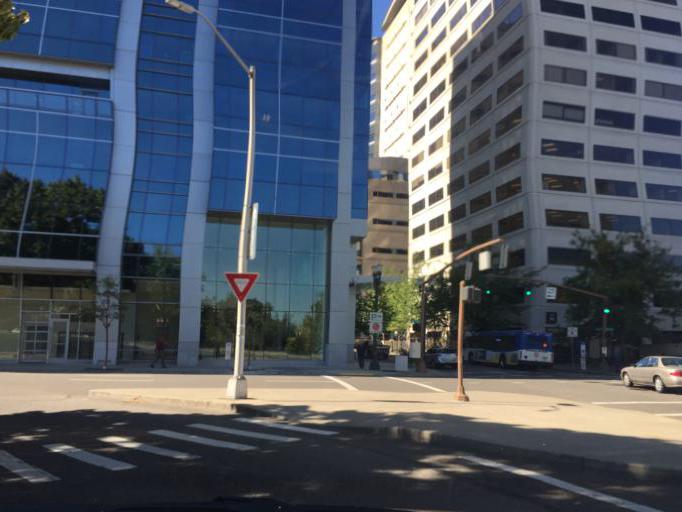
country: US
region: Oregon
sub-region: Multnomah County
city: Portland
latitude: 45.5148
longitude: -122.6748
